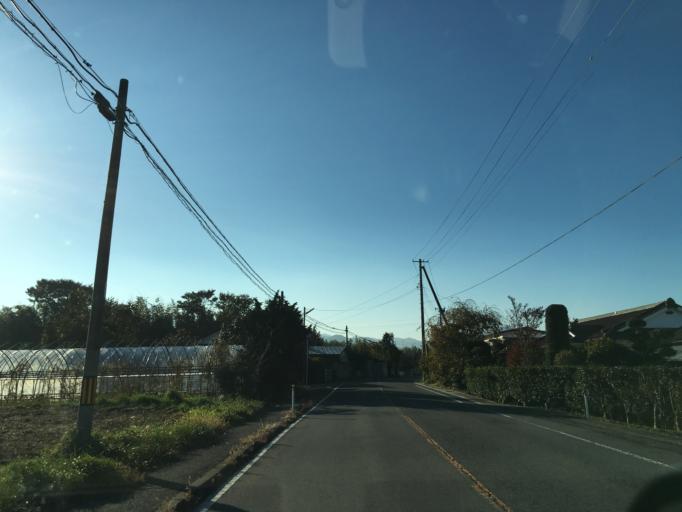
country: JP
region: Fukushima
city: Koriyama
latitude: 37.3930
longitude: 140.2794
